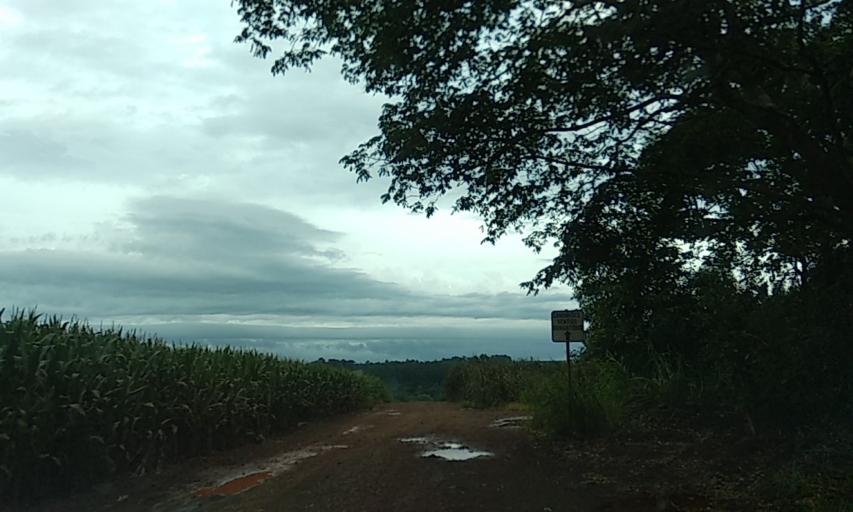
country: BR
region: Parana
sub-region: Marechal Candido Rondon
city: Marechal Candido Rondon
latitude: -24.5232
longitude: -54.0829
